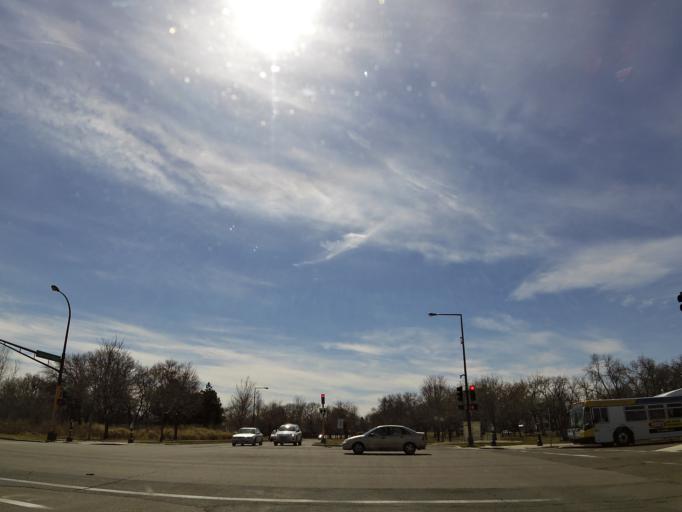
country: US
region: Minnesota
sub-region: Ramsey County
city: Saint Paul
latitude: 44.9778
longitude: -93.0472
